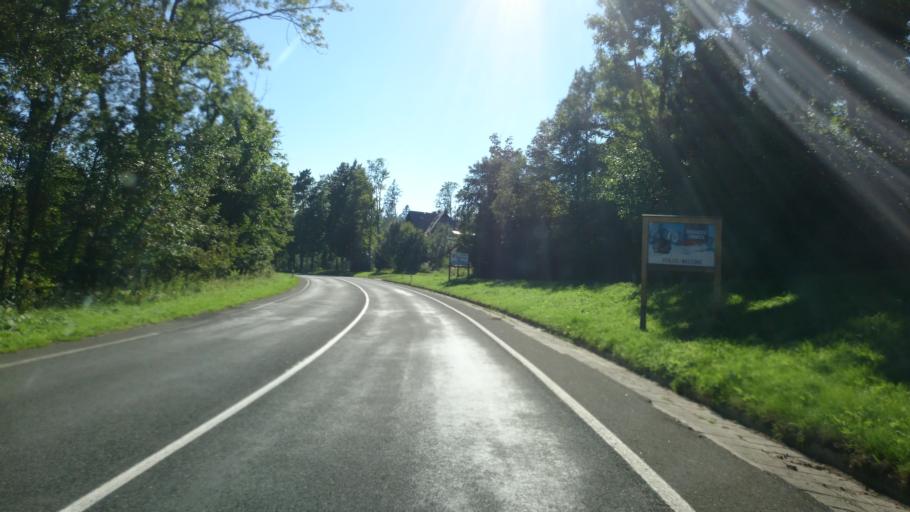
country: SK
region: Presovsky
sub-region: Okres Poprad
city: Nova Lesna
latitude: 49.1708
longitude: 20.2886
